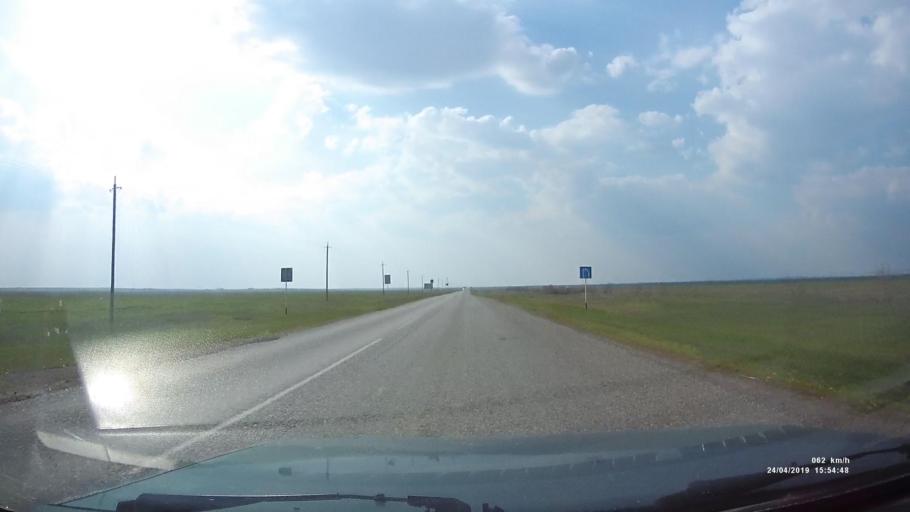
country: RU
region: Kalmykiya
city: Yashalta
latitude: 46.5863
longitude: 42.5610
